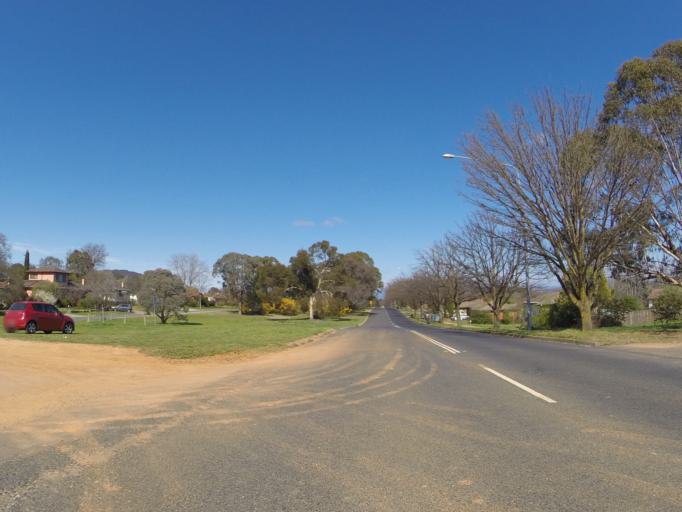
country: AU
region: Australian Capital Territory
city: Canberra
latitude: -35.2395
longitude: 149.1654
